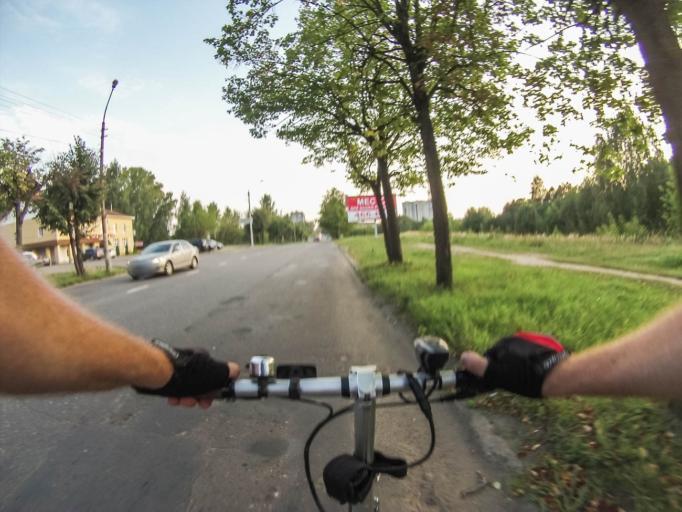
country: RU
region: Kostroma
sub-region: Kostromskoy Rayon
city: Kostroma
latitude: 57.7956
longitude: 40.9495
